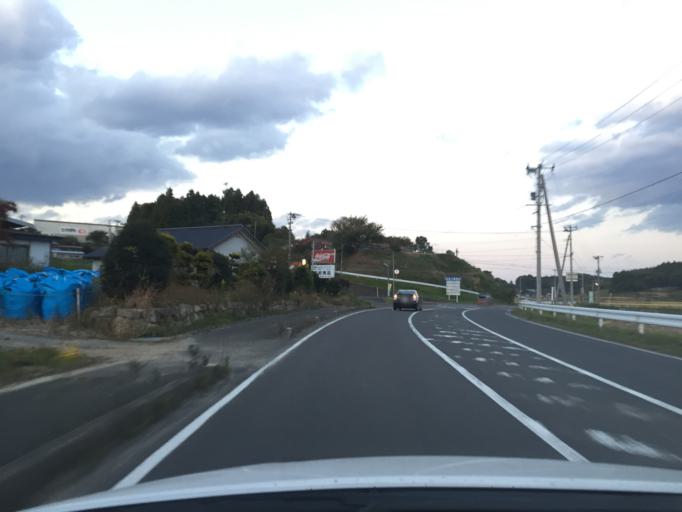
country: JP
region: Fukushima
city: Motomiya
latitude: 37.4927
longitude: 140.4524
